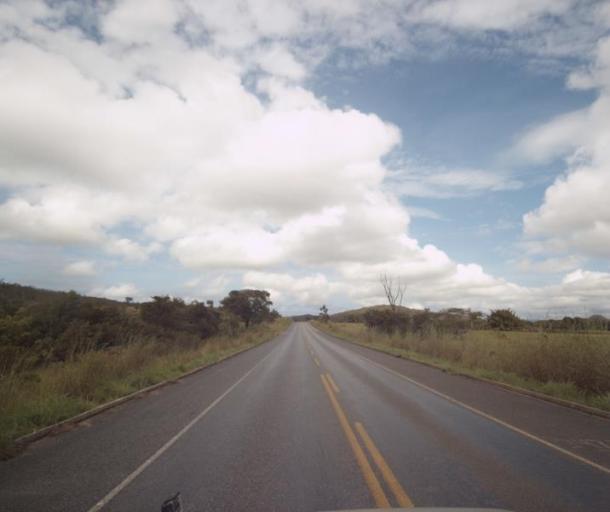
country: BR
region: Goias
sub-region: Pirenopolis
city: Pirenopolis
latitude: -15.6066
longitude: -48.6493
